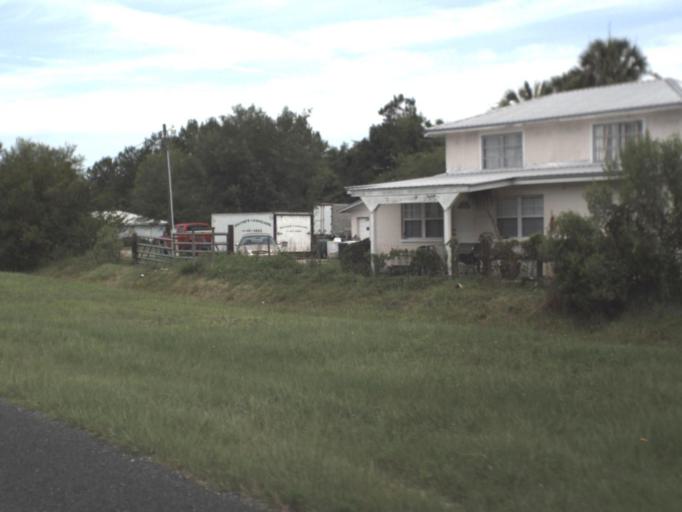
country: US
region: Florida
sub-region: Alachua County
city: Hawthorne
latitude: 29.5975
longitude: -82.1070
